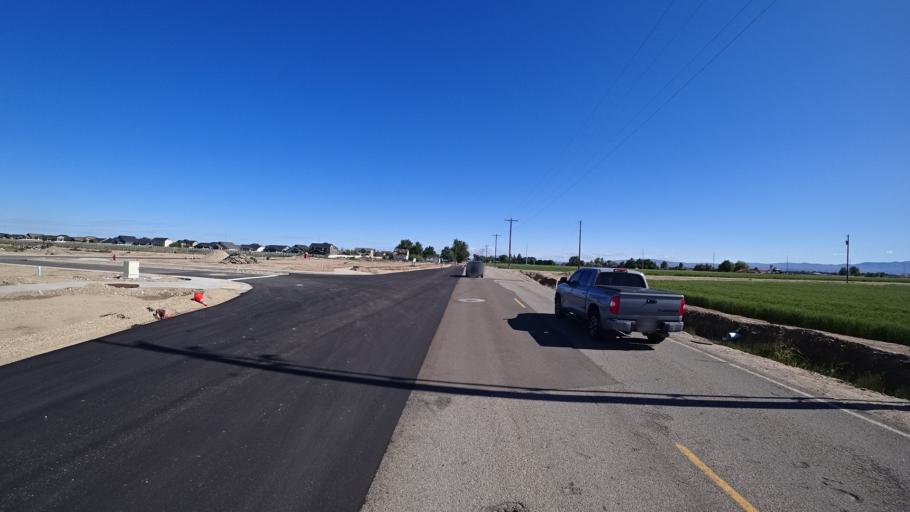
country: US
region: Idaho
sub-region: Ada County
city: Star
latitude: 43.6436
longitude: -116.4537
